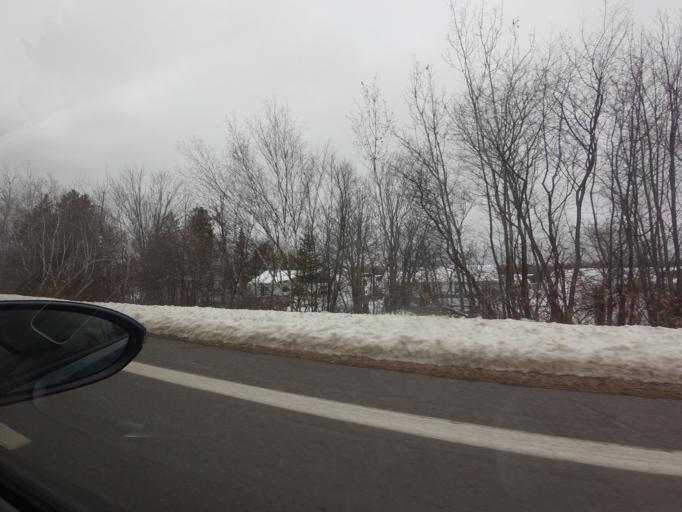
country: CA
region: New Brunswick
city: Oromocto
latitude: 45.8457
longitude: -66.5073
